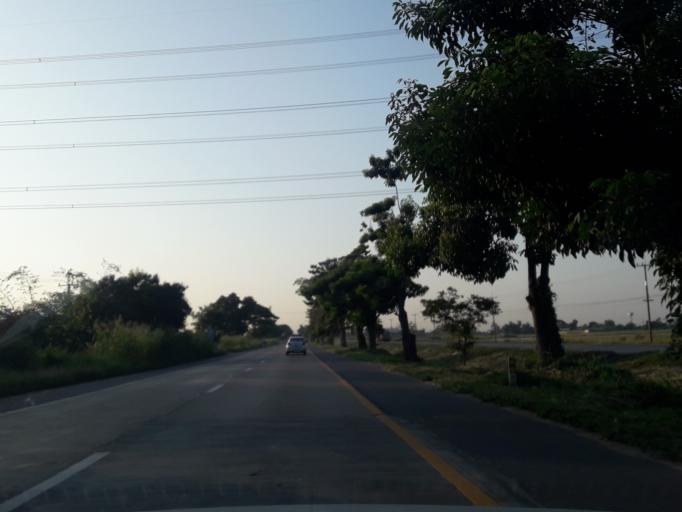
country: TH
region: Phra Nakhon Si Ayutthaya
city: Bang Pa-in
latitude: 14.2709
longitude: 100.5310
